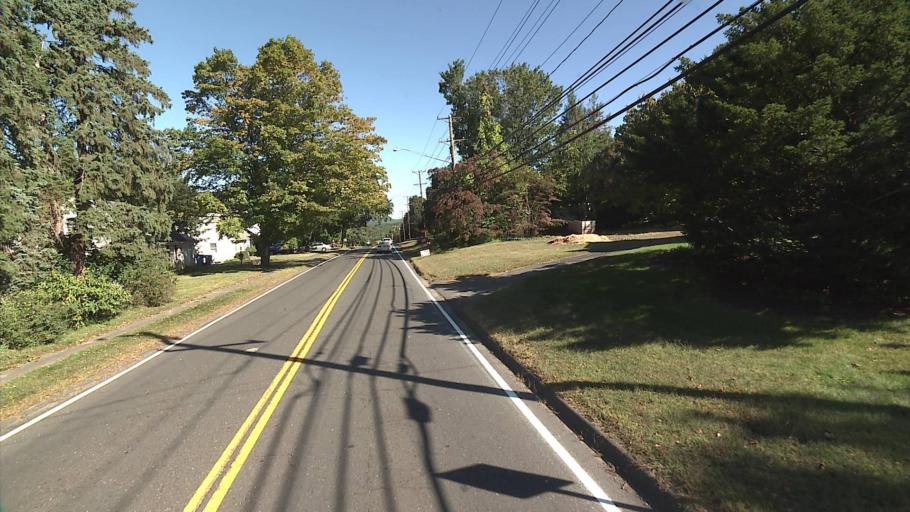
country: US
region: Connecticut
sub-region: Hartford County
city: Bristol
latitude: 41.6962
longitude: -72.9448
